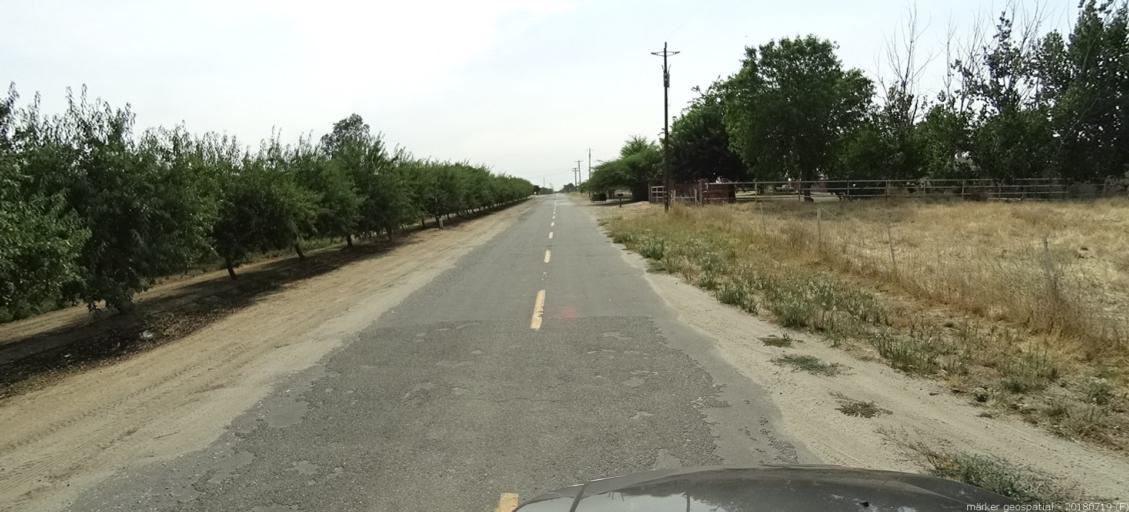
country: US
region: California
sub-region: Madera County
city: Fairmead
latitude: 37.1055
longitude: -120.2139
